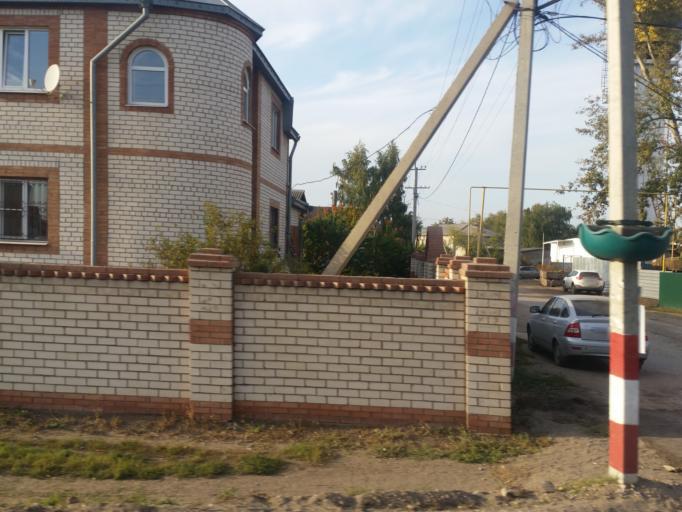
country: RU
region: Ulyanovsk
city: Cherdakly
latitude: 54.3554
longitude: 48.8529
